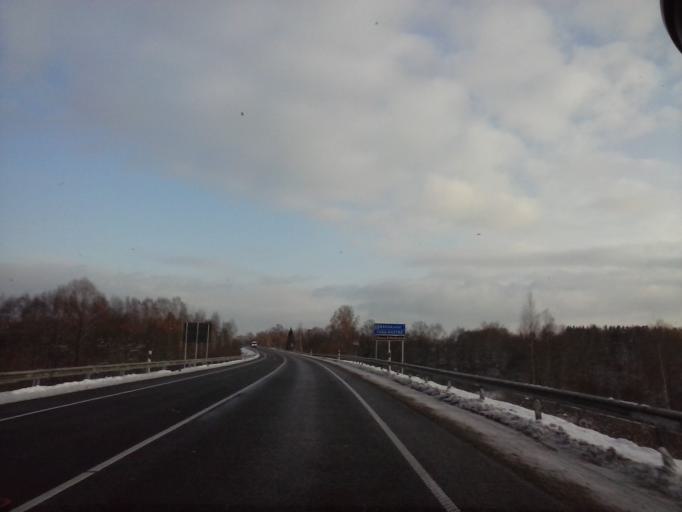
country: EE
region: Tartu
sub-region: Tartu linn
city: Tartu
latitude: 58.3585
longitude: 26.8970
